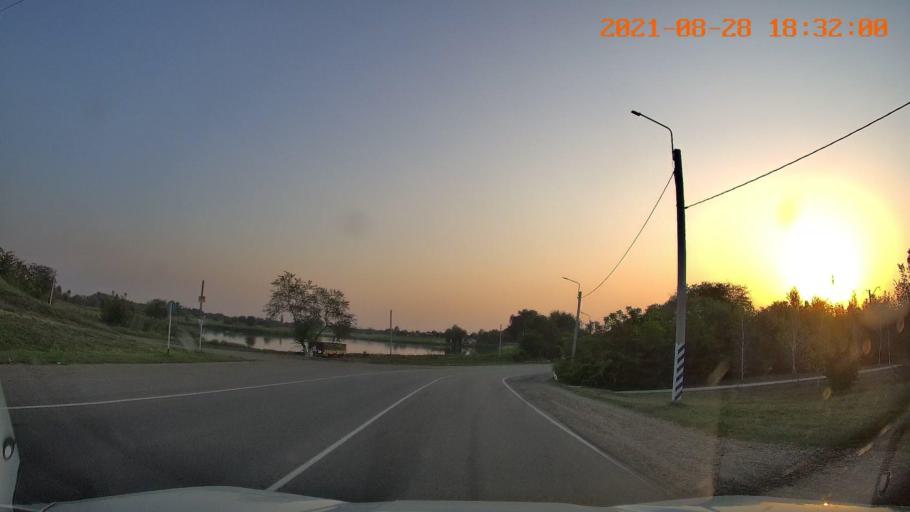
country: RU
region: Adygeya
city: Giaginskaya
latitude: 44.8779
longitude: 40.1957
